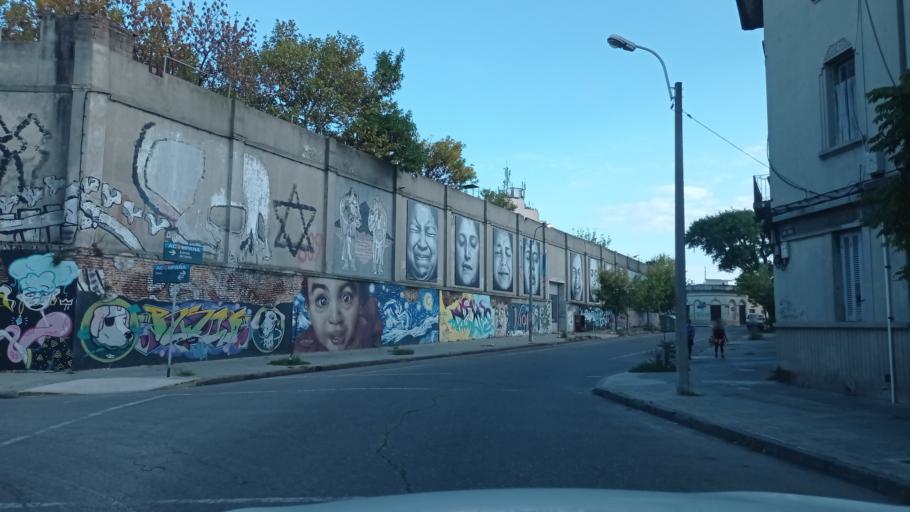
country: UY
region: Montevideo
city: Montevideo
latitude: -34.8935
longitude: -56.1809
